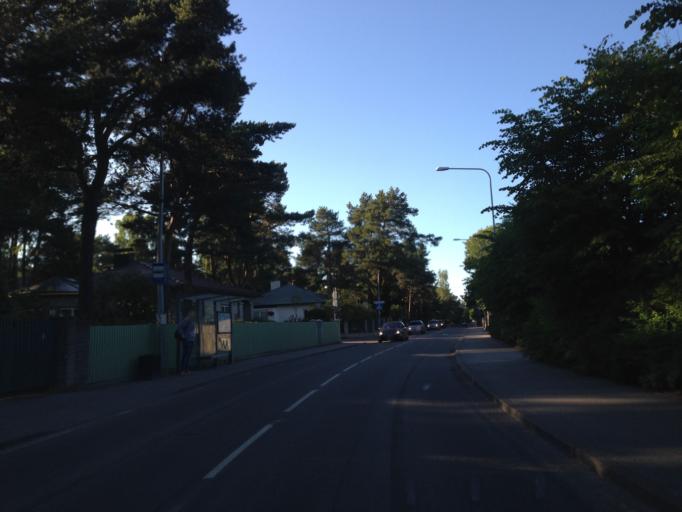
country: EE
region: Harju
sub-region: Saue vald
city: Laagri
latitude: 59.3649
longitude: 24.6292
